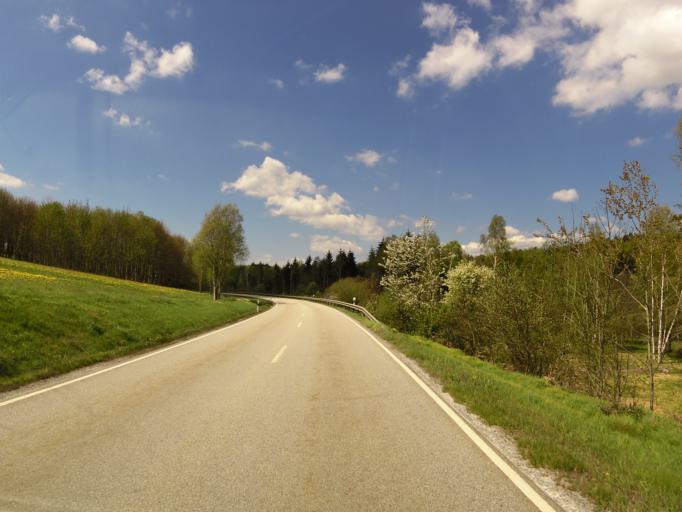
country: DE
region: Bavaria
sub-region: Lower Bavaria
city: Hinterschmiding
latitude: 48.8319
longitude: 13.5790
